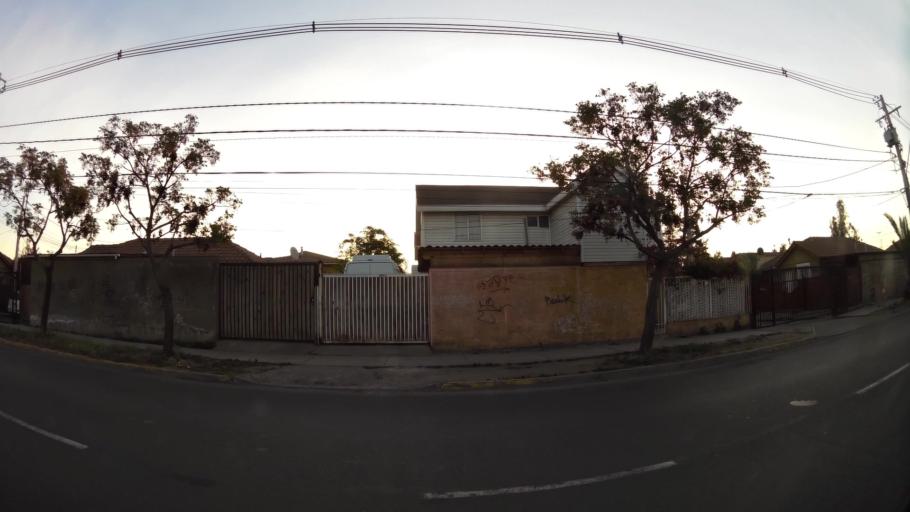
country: CL
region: Santiago Metropolitan
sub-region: Provincia de Cordillera
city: Puente Alto
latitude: -33.6006
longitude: -70.5883
